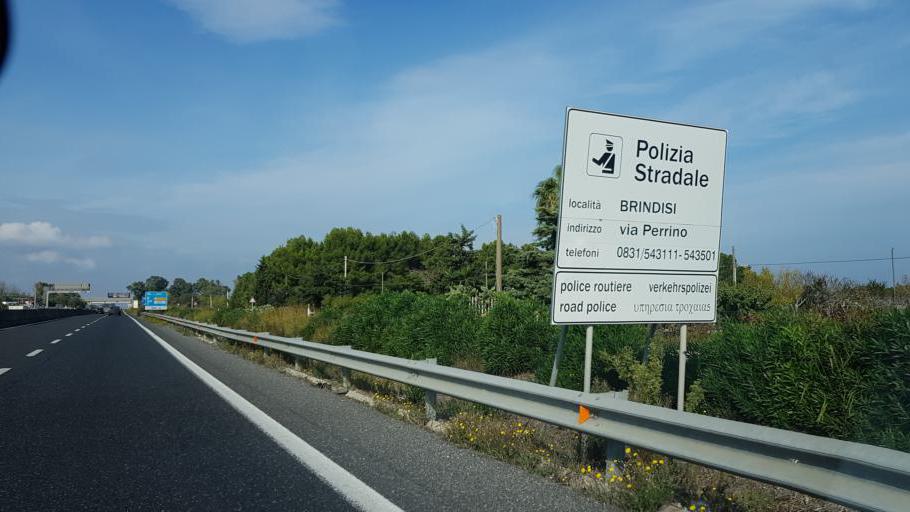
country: IT
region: Apulia
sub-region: Provincia di Brindisi
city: Brindisi
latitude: 40.6629
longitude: 17.8819
